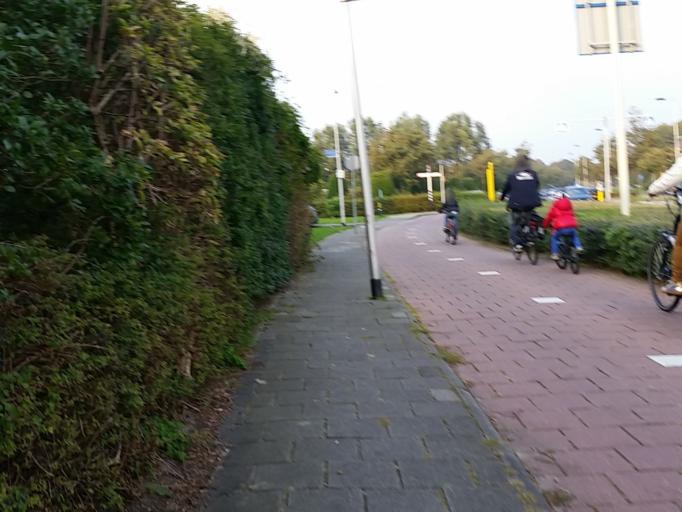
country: NL
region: South Holland
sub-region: Gemeente Noordwijk
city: Noordwijk-Binnen
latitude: 52.2292
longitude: 4.4455
